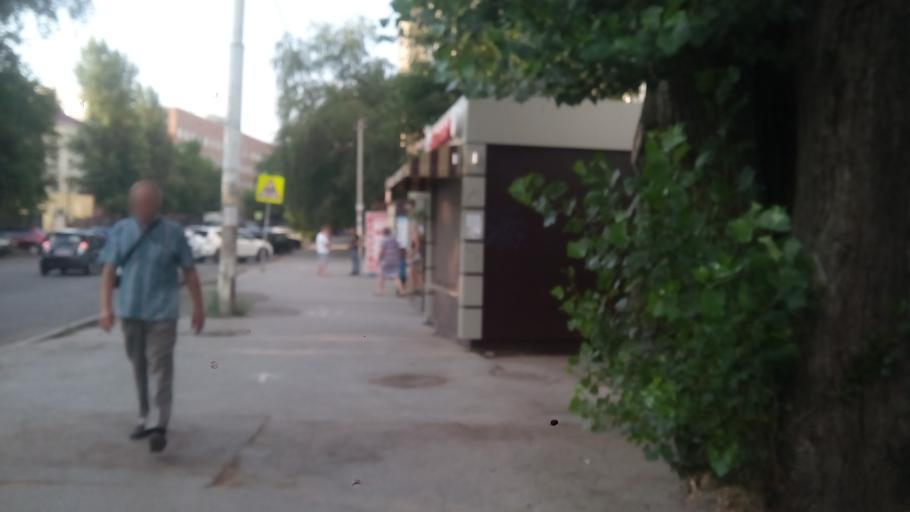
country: RU
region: Rostov
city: Imeni Chkalova
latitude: 47.2566
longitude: 39.7685
